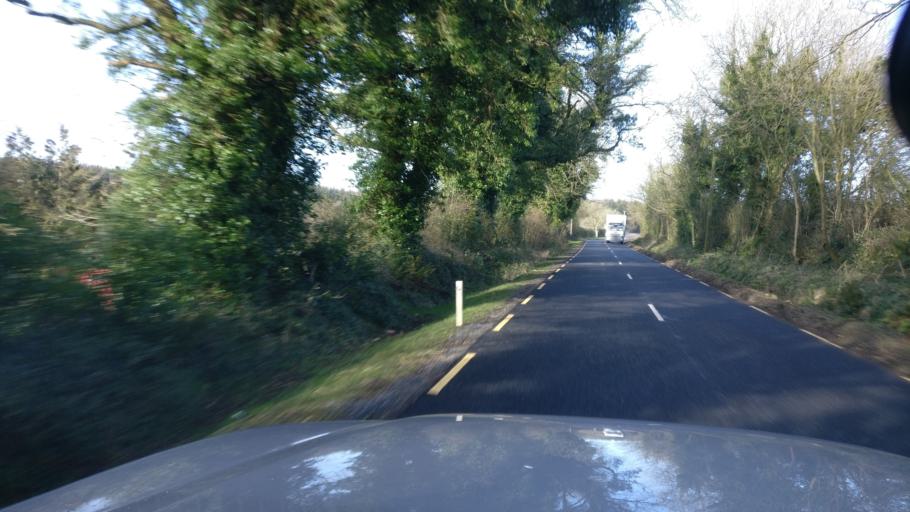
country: IE
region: Leinster
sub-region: Kilkenny
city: Castlecomer
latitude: 52.9075
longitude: -7.1829
